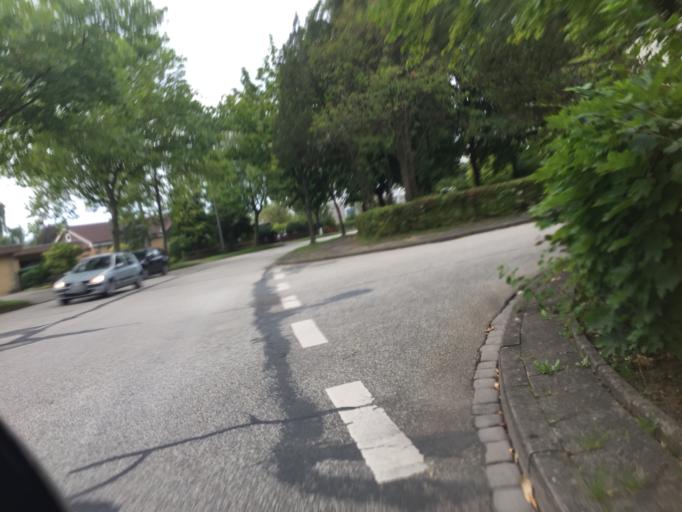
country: DE
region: Schleswig-Holstein
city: Ottenbuttel
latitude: 53.9465
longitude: 9.5050
